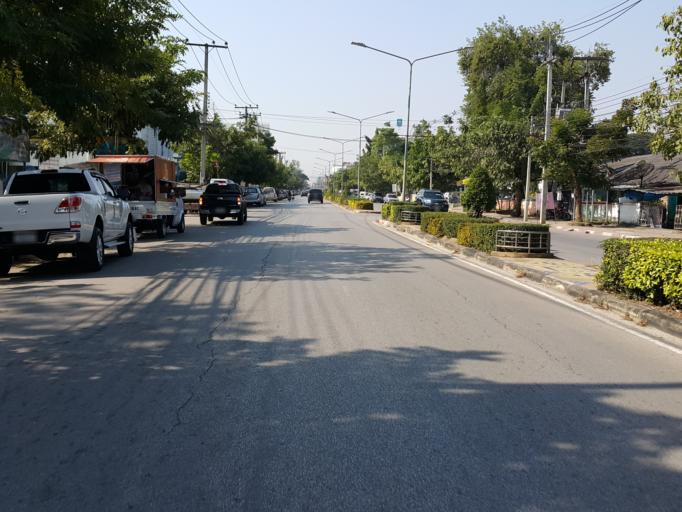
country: TH
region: Lampang
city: Lampang
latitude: 18.2895
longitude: 99.5081
